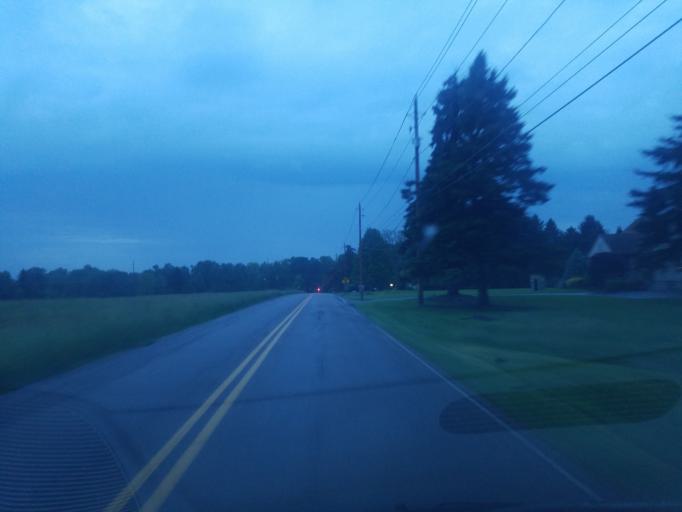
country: US
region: Ohio
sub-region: Mahoning County
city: Boardman
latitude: 40.9909
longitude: -80.7114
